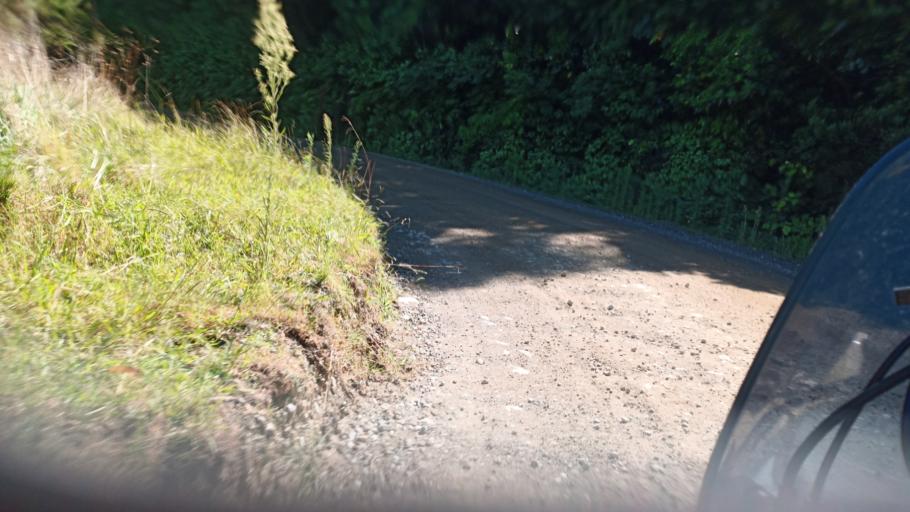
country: NZ
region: Gisborne
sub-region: Gisborne District
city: Gisborne
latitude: -38.3929
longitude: 177.6685
